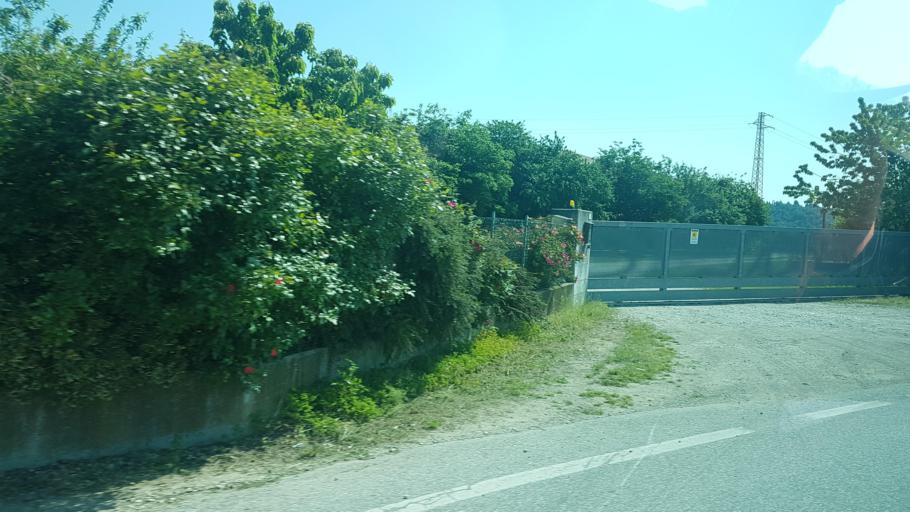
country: IT
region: Veneto
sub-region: Provincia di Treviso
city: Bigolino
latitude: 45.8702
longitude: 12.0183
